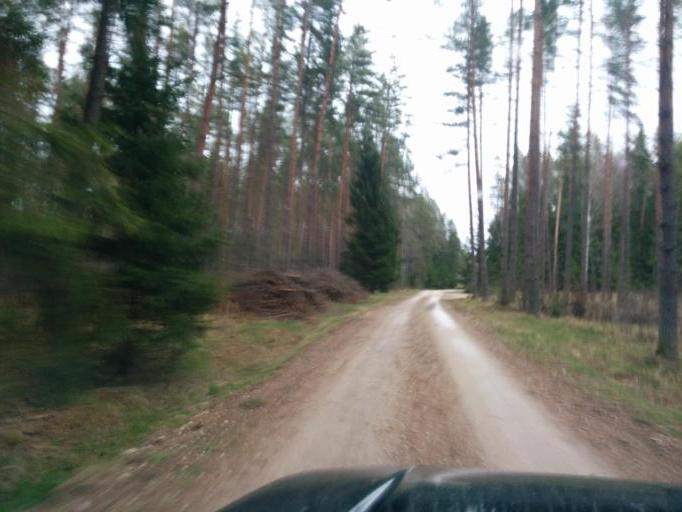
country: LV
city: Tireli
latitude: 56.8083
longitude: 23.6800
